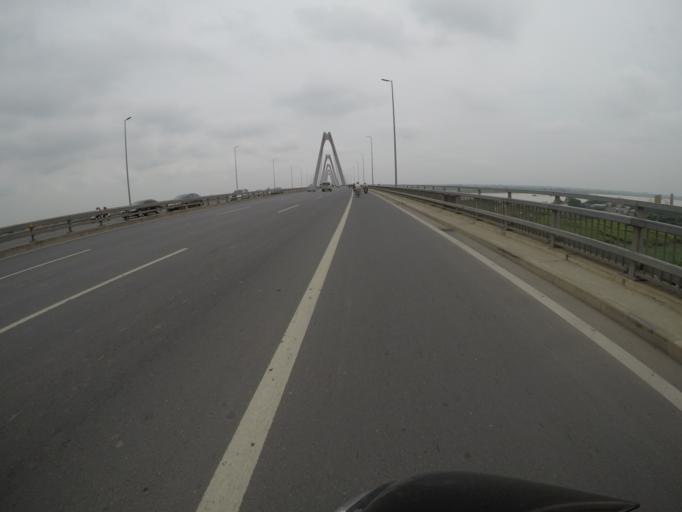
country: VN
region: Ha Noi
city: Tay Ho
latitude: 21.0862
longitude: 105.8175
